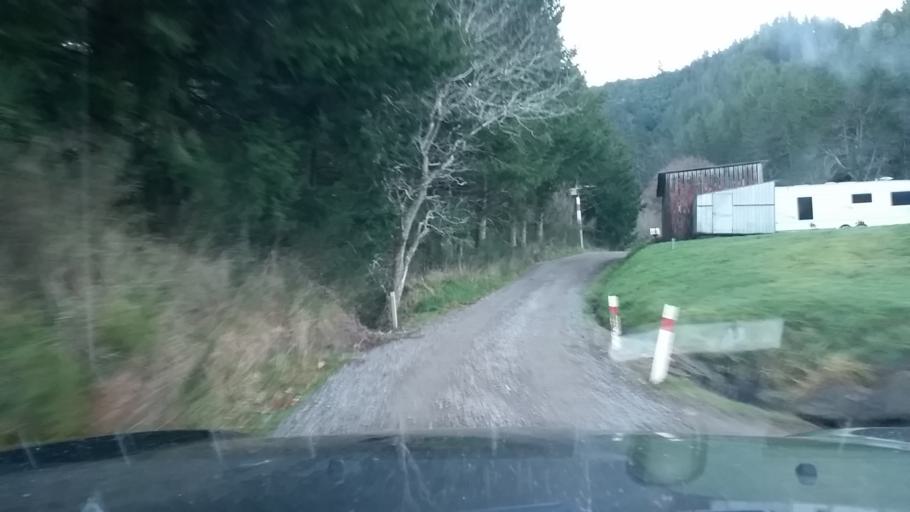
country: NZ
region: Marlborough
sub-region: Marlborough District
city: Blenheim
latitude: -41.4697
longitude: 173.7442
